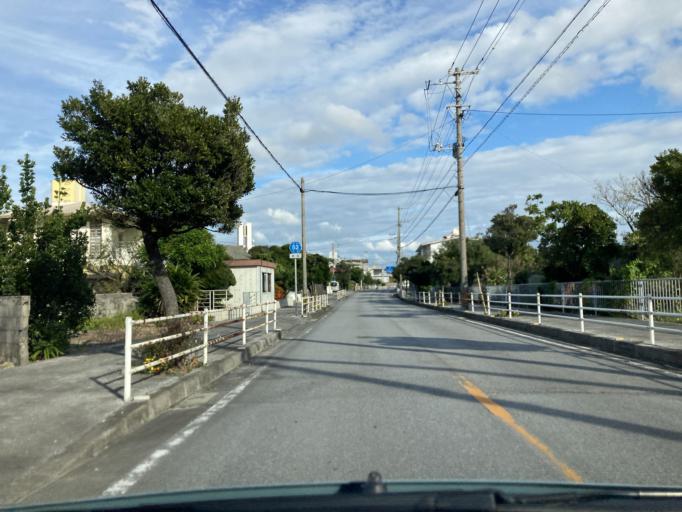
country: JP
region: Okinawa
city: Itoman
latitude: 26.1337
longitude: 127.7290
